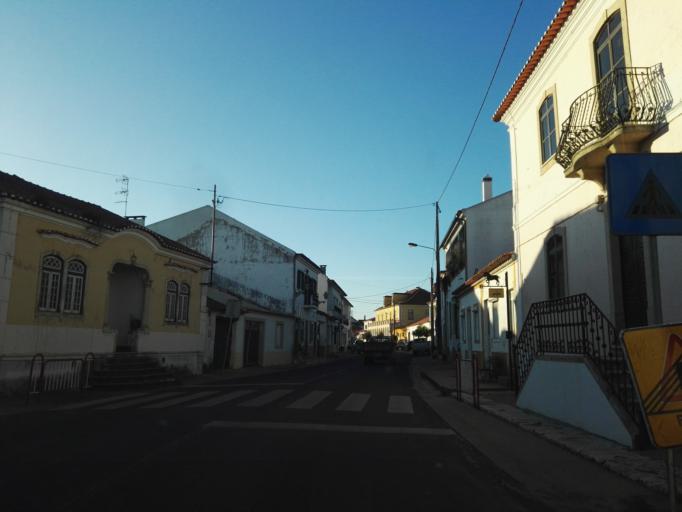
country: PT
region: Santarem
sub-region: Alpiarca
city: Alpiarca
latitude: 39.3420
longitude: -8.5551
